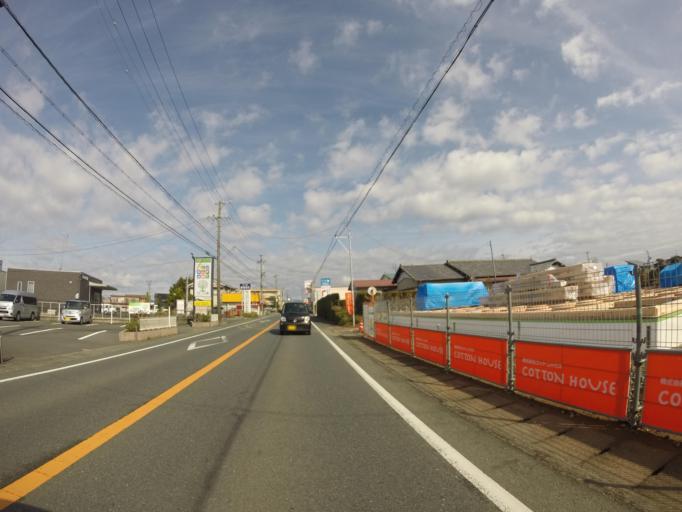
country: JP
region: Shizuoka
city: Hamakita
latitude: 34.7875
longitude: 137.7058
